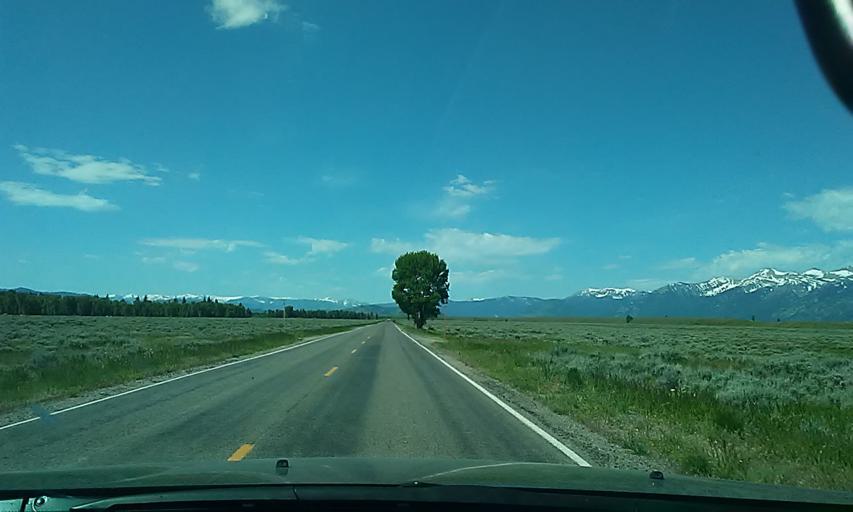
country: US
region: Wyoming
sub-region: Teton County
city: Jackson
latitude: 43.6181
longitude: -110.6736
